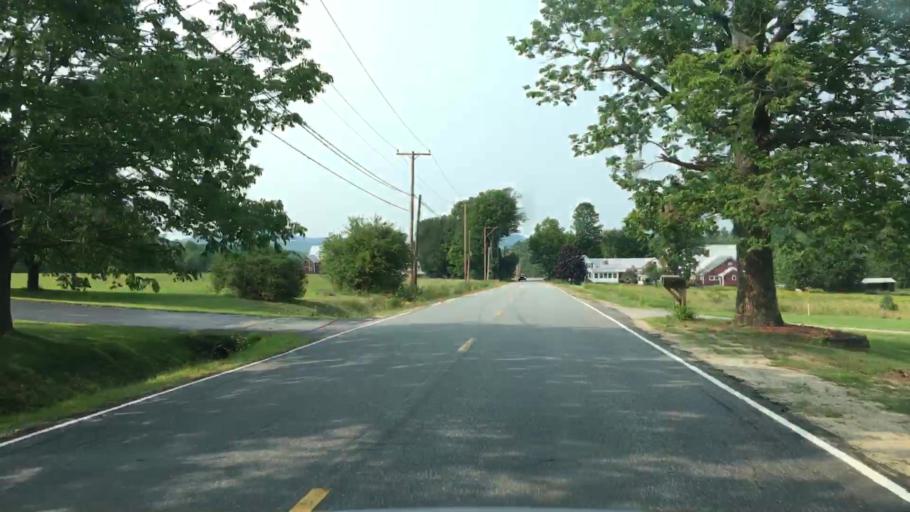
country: US
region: Maine
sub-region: Oxford County
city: Norway
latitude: 44.2249
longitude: -70.5934
